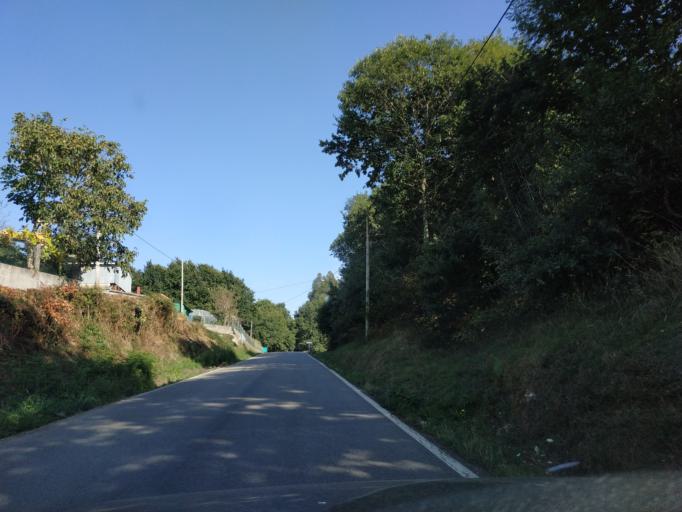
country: ES
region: Galicia
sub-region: Provincia da Coruna
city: Cerceda
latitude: 43.2339
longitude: -8.4843
